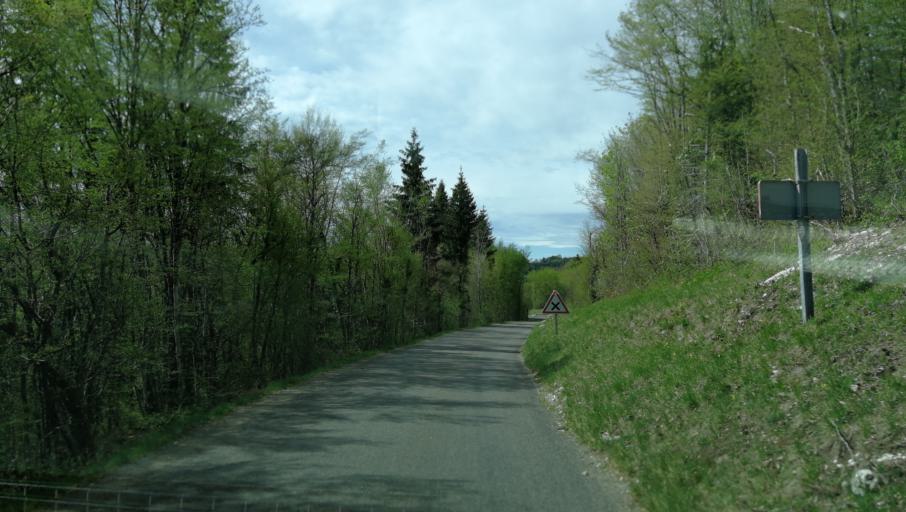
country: FR
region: Rhone-Alpes
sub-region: Departement de l'Ain
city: Arbent
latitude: 46.2306
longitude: 5.7537
